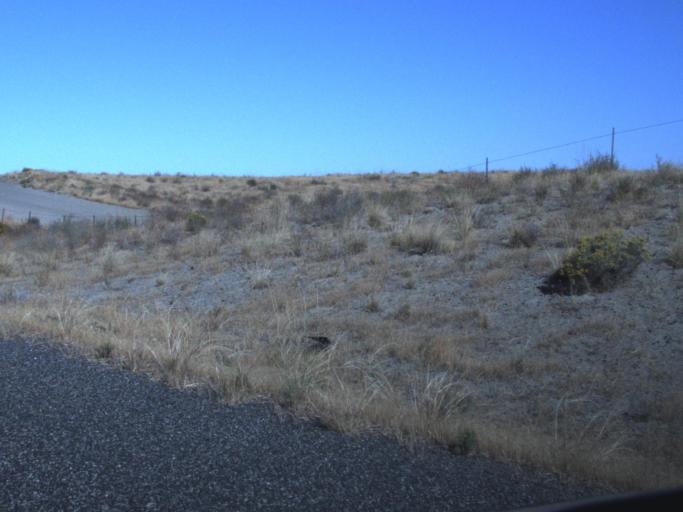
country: US
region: Washington
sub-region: Benton County
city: Benton City
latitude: 46.4950
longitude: -119.6008
